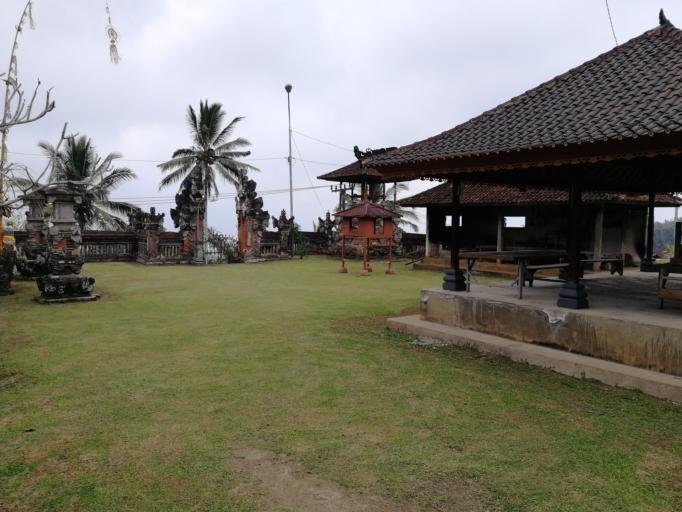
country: ID
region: Bali
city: Banjar Asahduren
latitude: -8.3864
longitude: 114.8731
